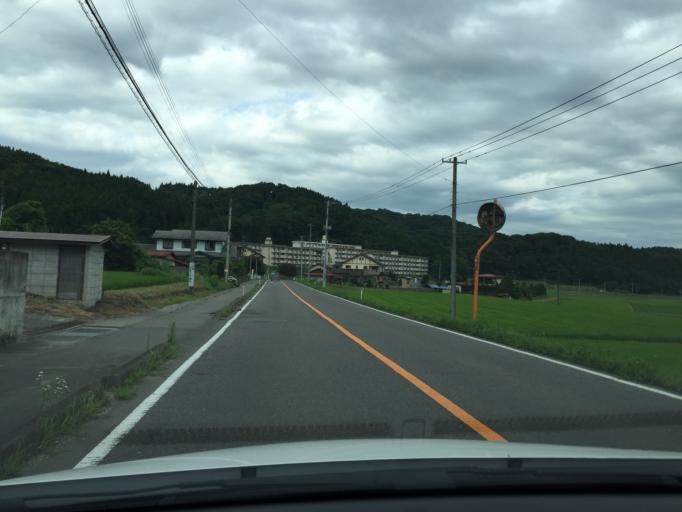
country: JP
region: Fukushima
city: Sukagawa
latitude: 37.1932
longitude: 140.2278
